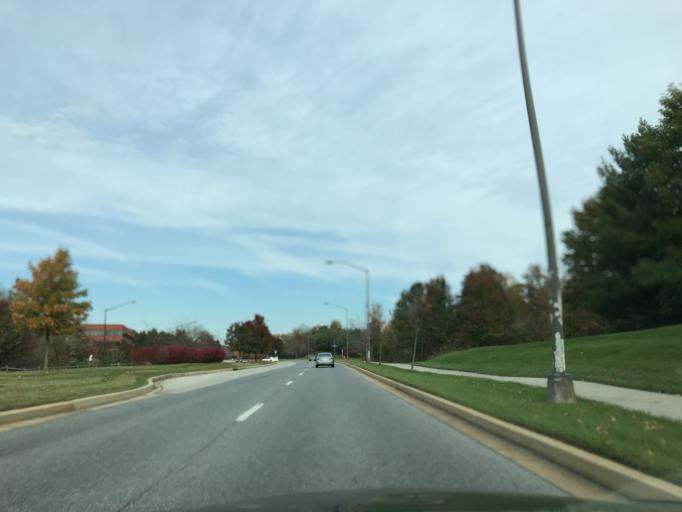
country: US
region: Maryland
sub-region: Howard County
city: Columbia
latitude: 39.1974
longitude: -76.8082
